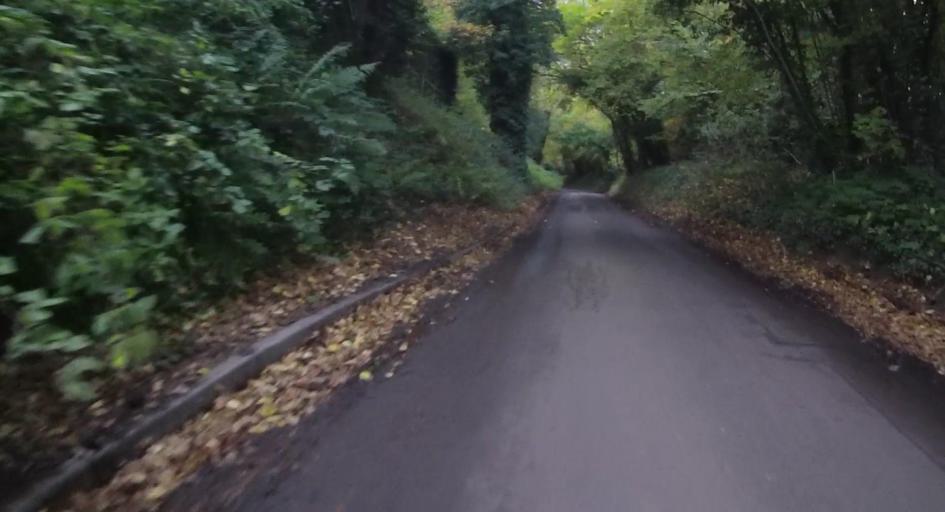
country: GB
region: England
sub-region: Hampshire
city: Lindford
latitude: 51.1323
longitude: -0.8242
